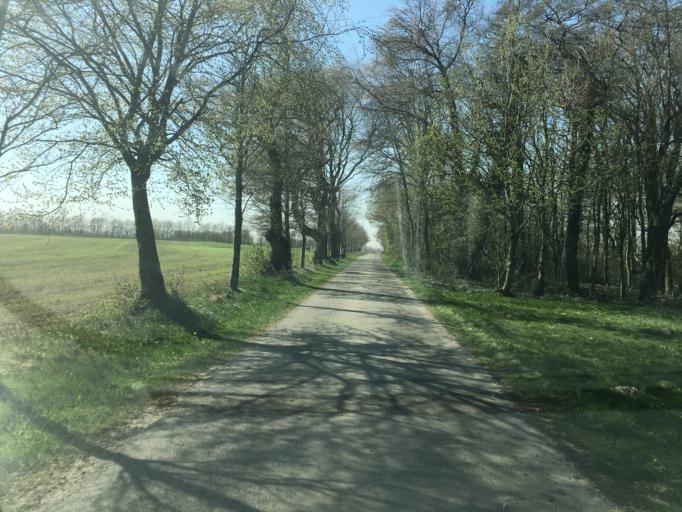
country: DK
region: South Denmark
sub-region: Aabenraa Kommune
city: Rodekro
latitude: 55.1055
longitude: 9.2353
